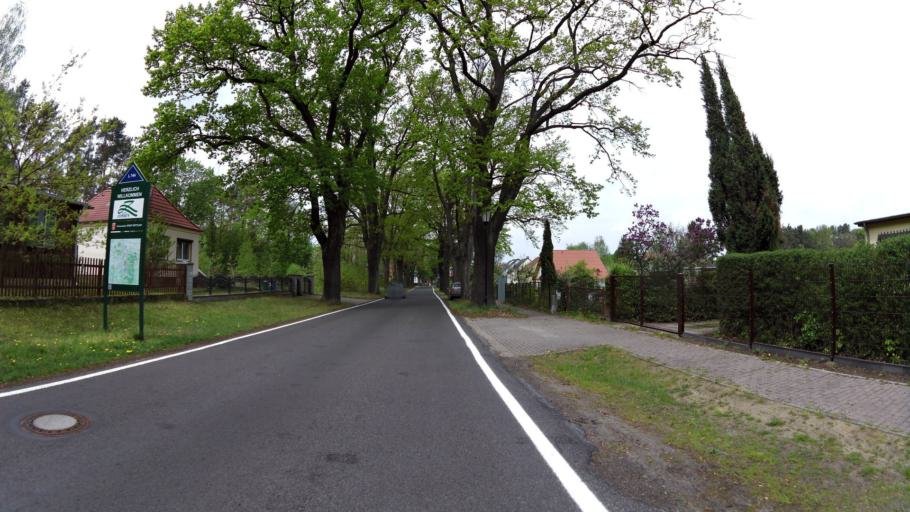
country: DE
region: Brandenburg
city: Mittenwalde
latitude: 52.2075
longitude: 13.5647
